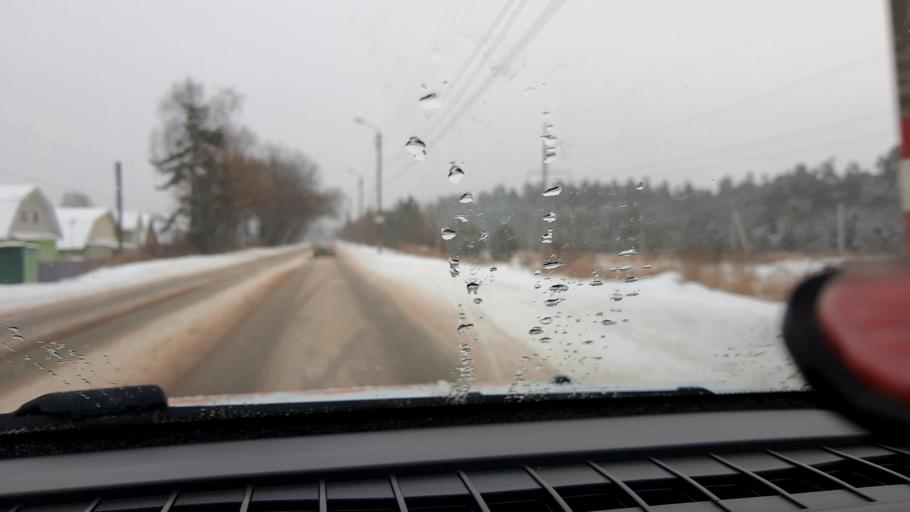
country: RU
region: Nizjnij Novgorod
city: Bor
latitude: 56.3284
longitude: 44.1266
